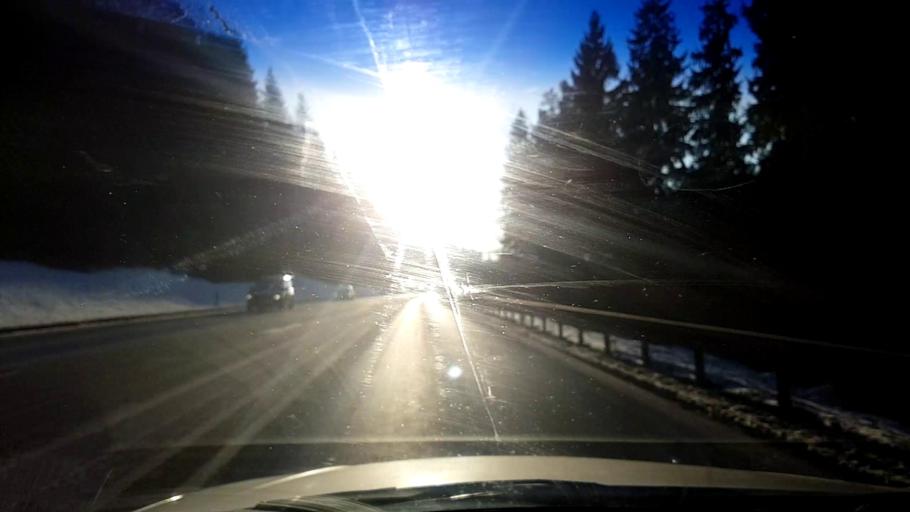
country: DE
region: Bavaria
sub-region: Upper Franconia
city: Bischofsgrun
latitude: 50.0513
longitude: 11.7722
